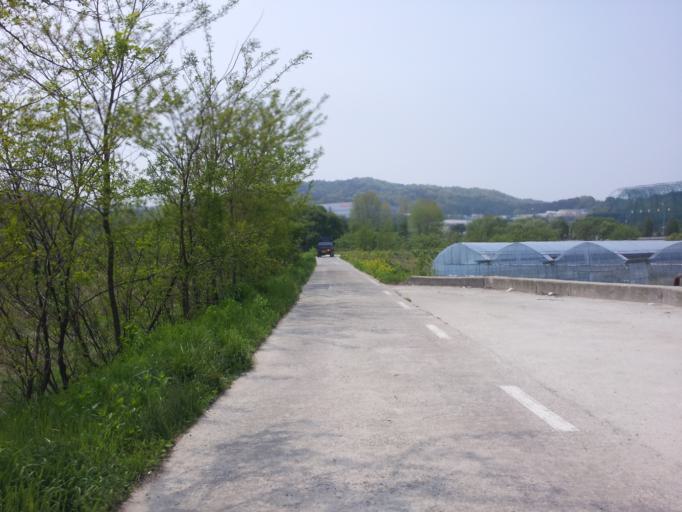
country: KR
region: Daejeon
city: Daejeon
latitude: 36.2570
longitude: 127.2837
